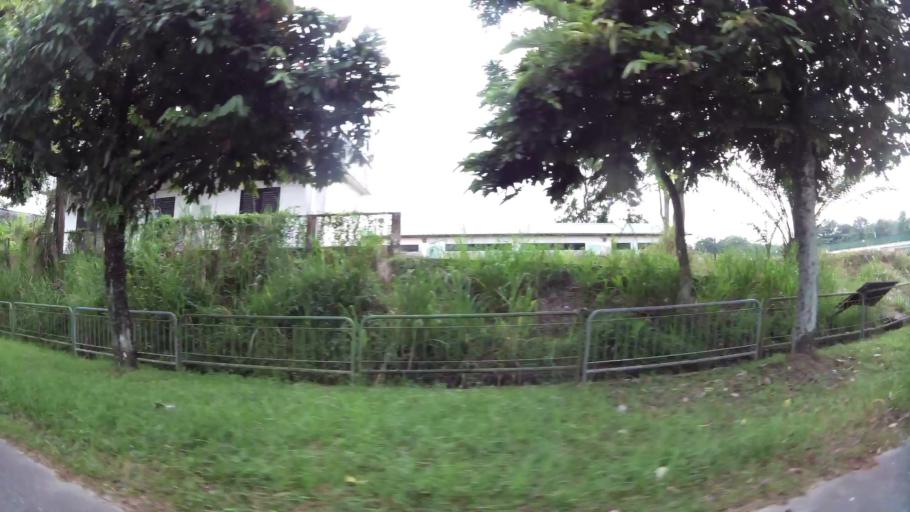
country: MY
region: Johor
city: Johor Bahru
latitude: 1.4359
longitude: 103.7099
